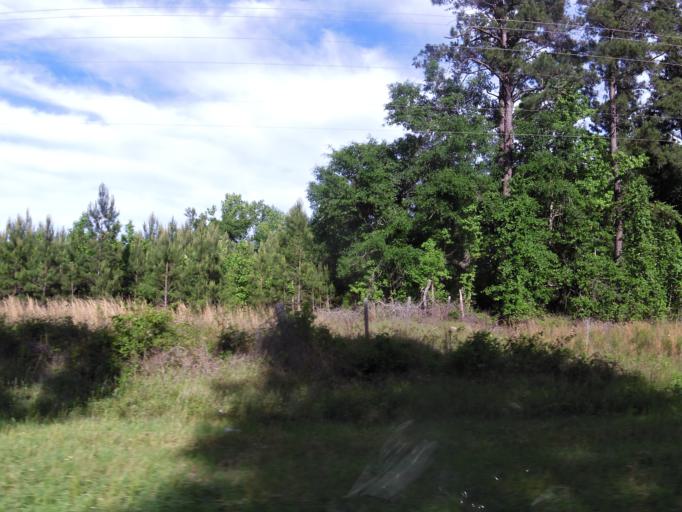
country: US
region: South Carolina
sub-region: Allendale County
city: Fairfax
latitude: 32.9182
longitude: -81.2374
